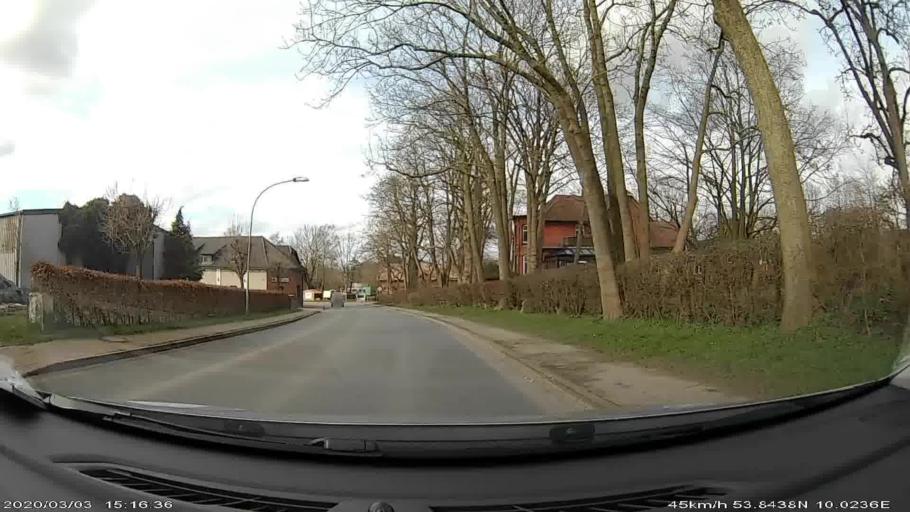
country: DE
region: Schleswig-Holstein
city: Kattendorf
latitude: 53.8436
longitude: 10.0236
